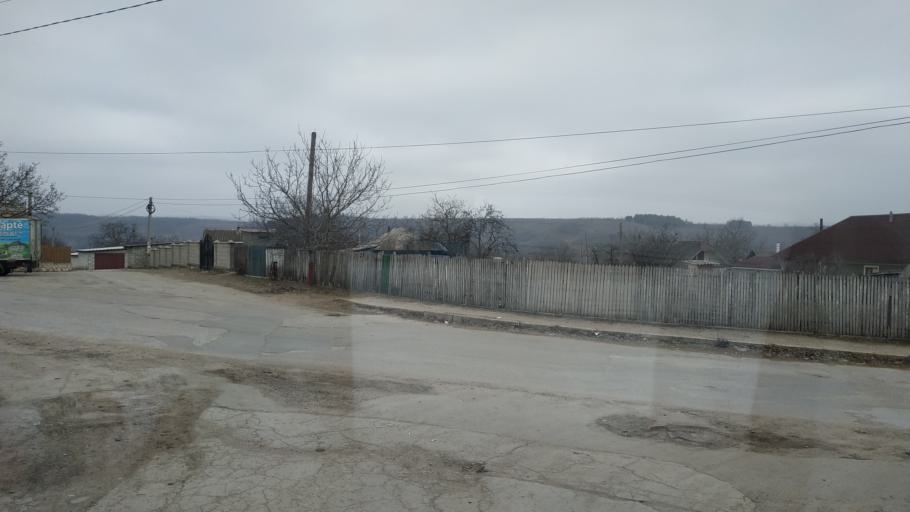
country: MD
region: Hincesti
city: Hincesti
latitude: 46.8918
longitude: 28.4129
